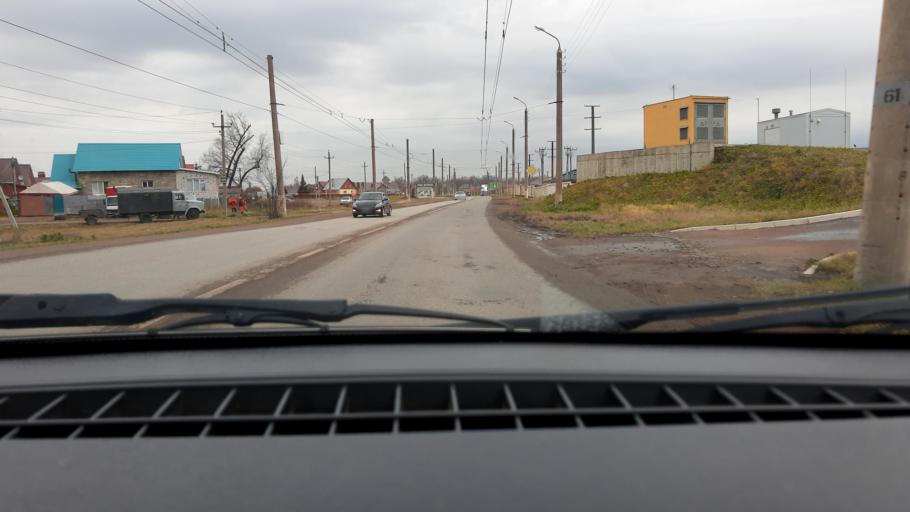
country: RU
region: Bashkortostan
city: Ufa
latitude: 54.7823
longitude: 55.9476
